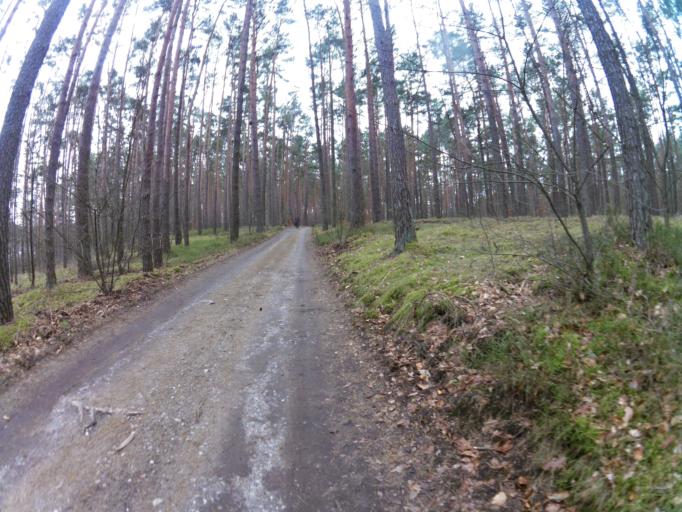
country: PL
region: West Pomeranian Voivodeship
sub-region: Powiat mysliborski
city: Debno
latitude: 52.7675
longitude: 14.8069
